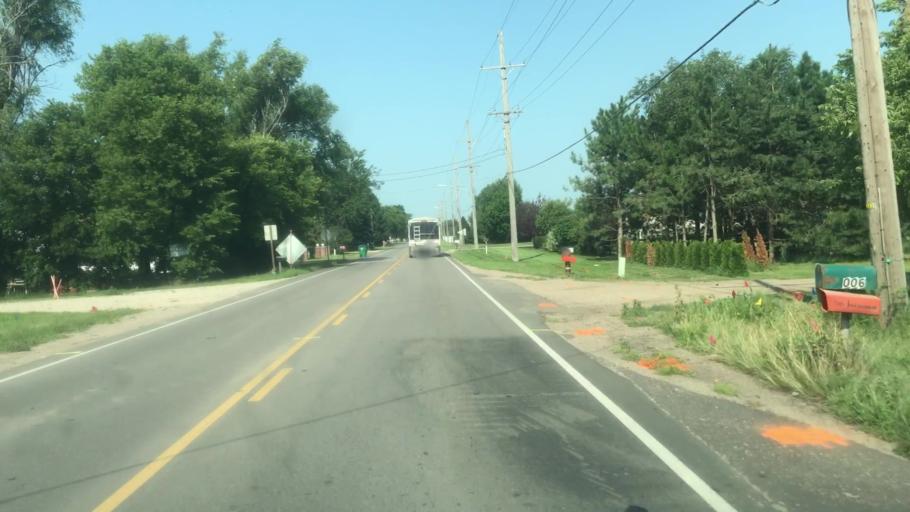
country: US
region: Nebraska
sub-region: Hall County
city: Grand Island
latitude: 40.9456
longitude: -98.3345
